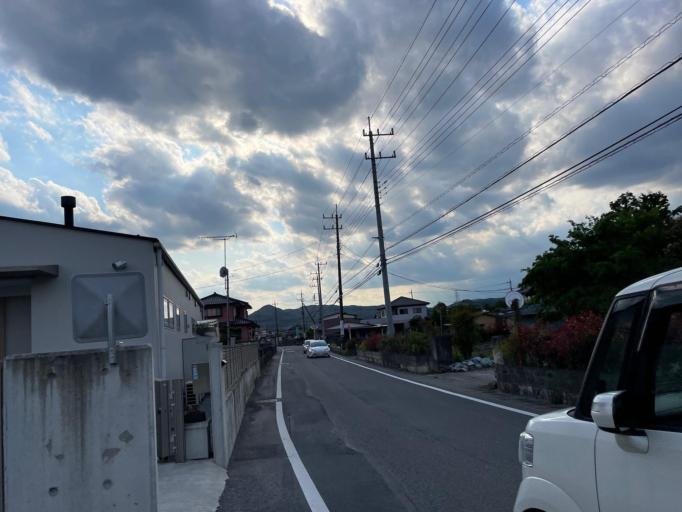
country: JP
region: Tochigi
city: Tochigi
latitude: 36.4114
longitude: 139.7080
